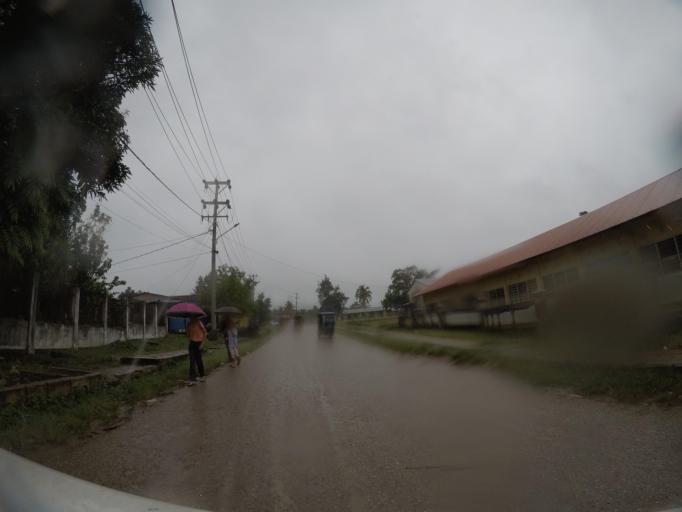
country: TL
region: Lautem
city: Lospalos
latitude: -8.5227
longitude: 126.9959
